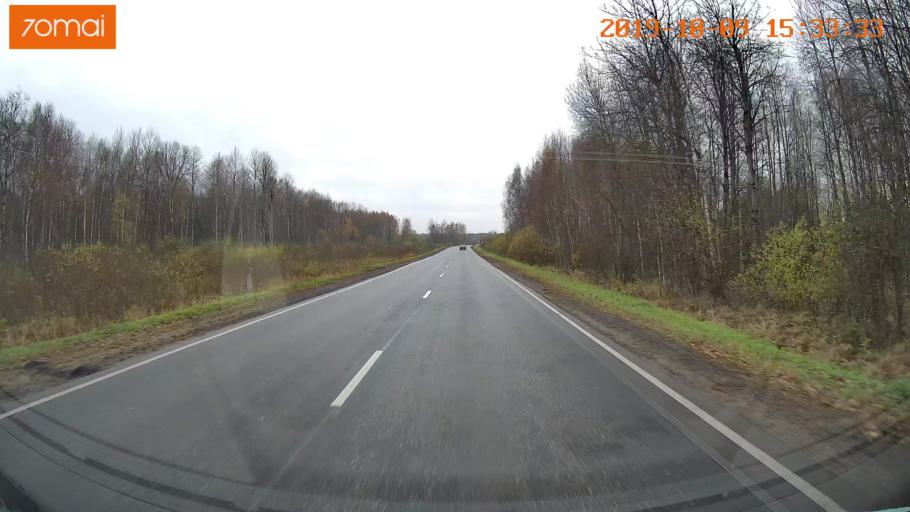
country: RU
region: Kostroma
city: Oktyabr'skiy
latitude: 57.9501
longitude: 41.2609
